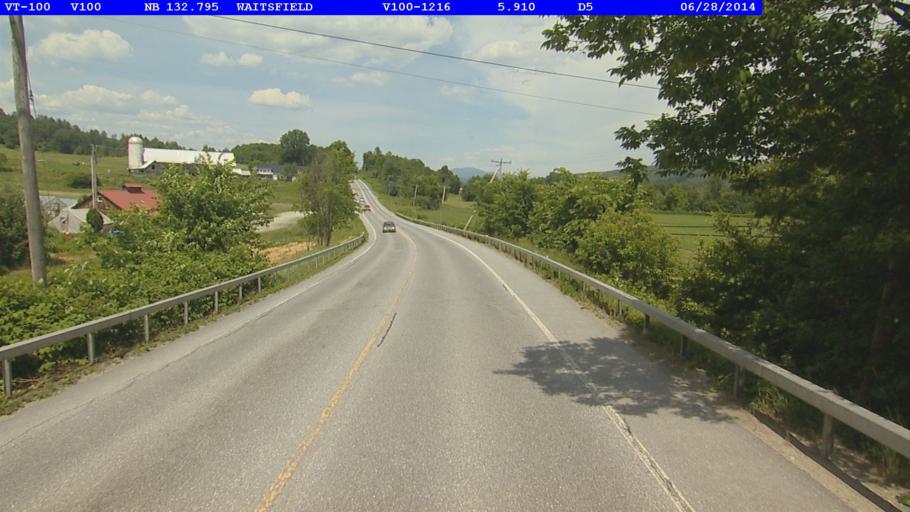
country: US
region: Vermont
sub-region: Washington County
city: Waterbury
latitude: 44.2133
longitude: -72.7935
